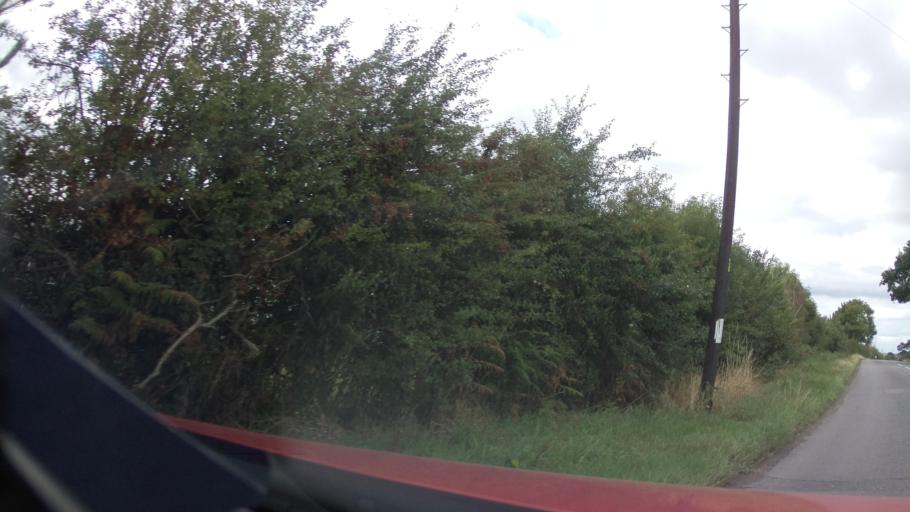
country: GB
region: England
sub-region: Nottinghamshire
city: East Leake
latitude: 52.8214
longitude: -1.1759
